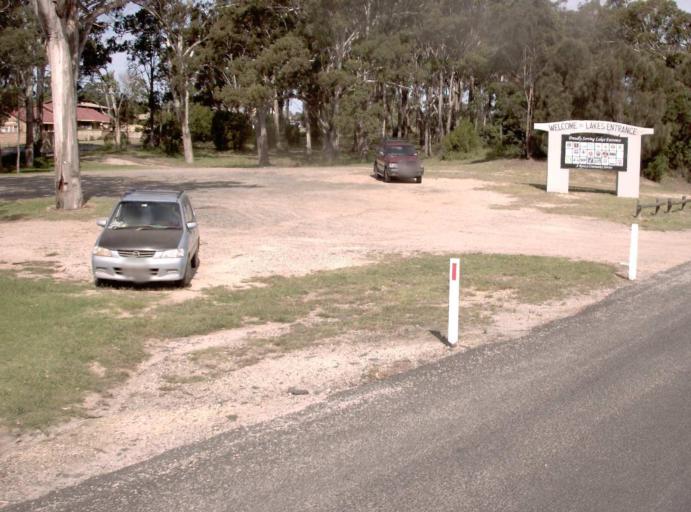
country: AU
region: Victoria
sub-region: East Gippsland
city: Lakes Entrance
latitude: -37.8792
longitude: 147.9617
